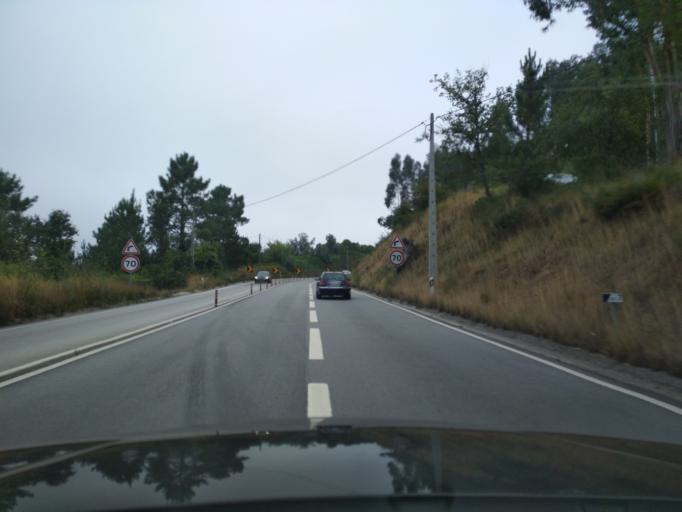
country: PT
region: Aveiro
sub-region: Mealhada
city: Pampilhosa do Botao
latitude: 40.2782
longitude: -8.4458
